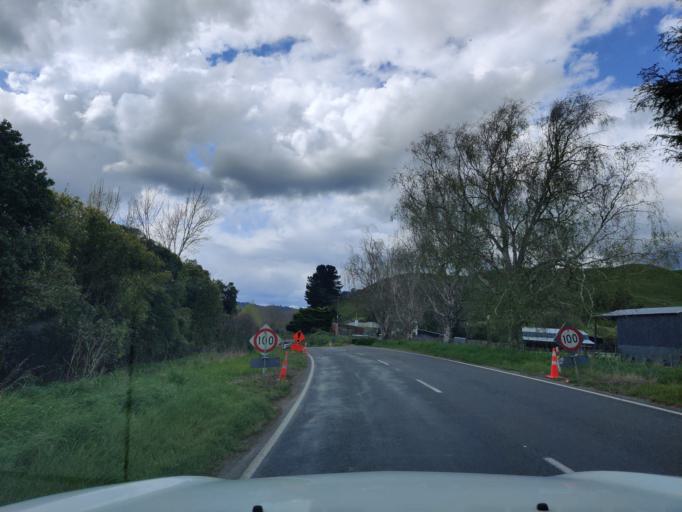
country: NZ
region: Manawatu-Wanganui
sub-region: Wanganui District
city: Wanganui
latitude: -39.8748
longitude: 175.1118
